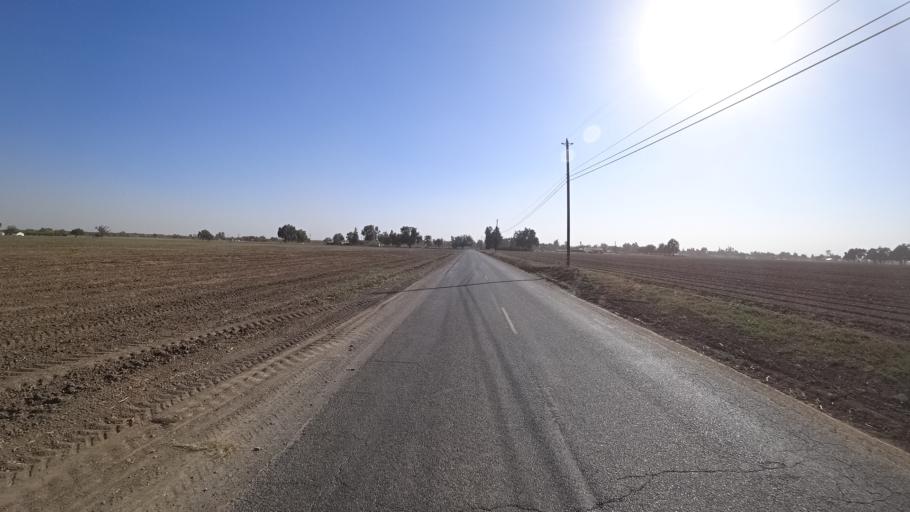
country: US
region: California
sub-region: Yolo County
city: Woodland
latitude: 38.7406
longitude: -121.8033
